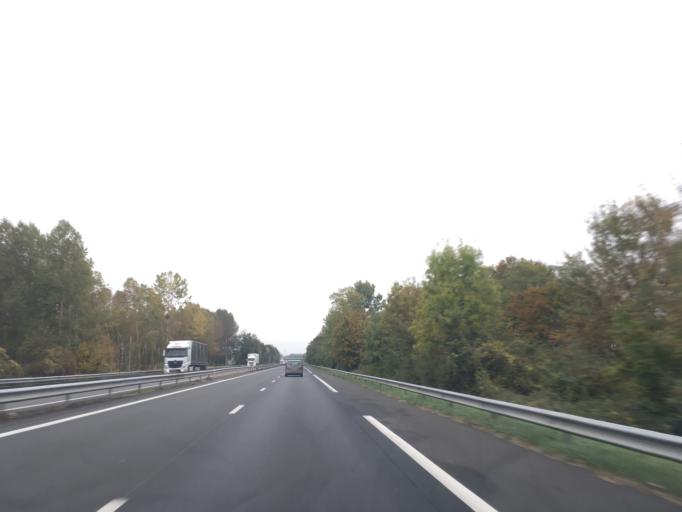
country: FR
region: Pays de la Loire
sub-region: Departement de Maine-et-Loire
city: Seiches-sur-le-Loir
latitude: 47.5896
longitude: -0.3232
